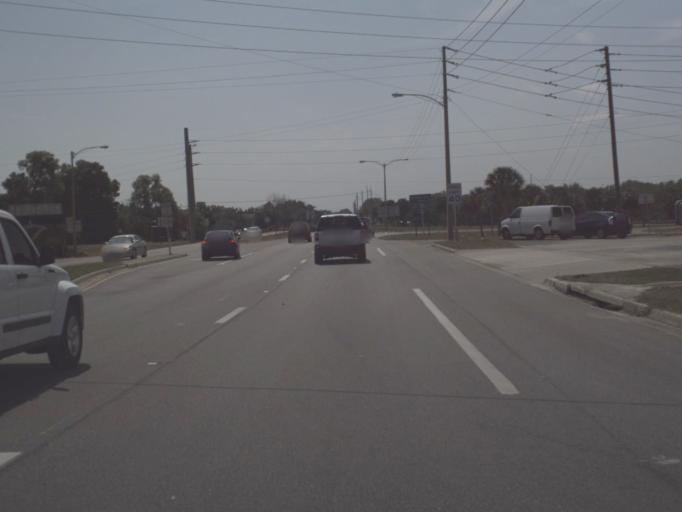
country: US
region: Florida
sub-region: Lake County
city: Eustis
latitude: 28.8261
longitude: -81.6856
